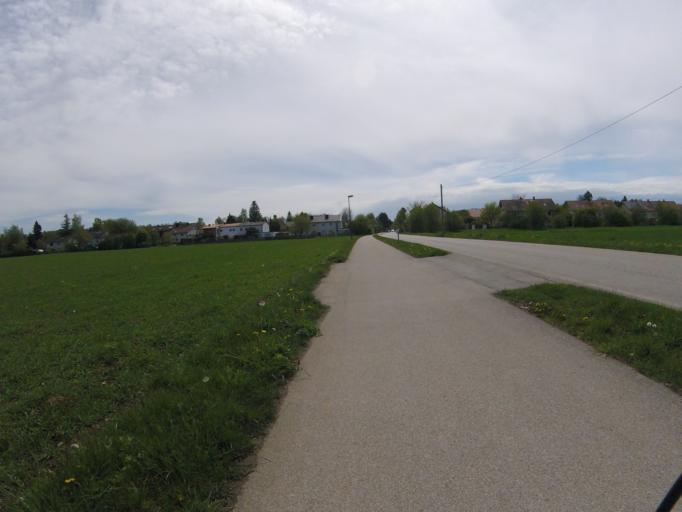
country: DE
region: Bavaria
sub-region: Upper Bavaria
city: Hohenbrunn
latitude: 48.0366
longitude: 11.7053
